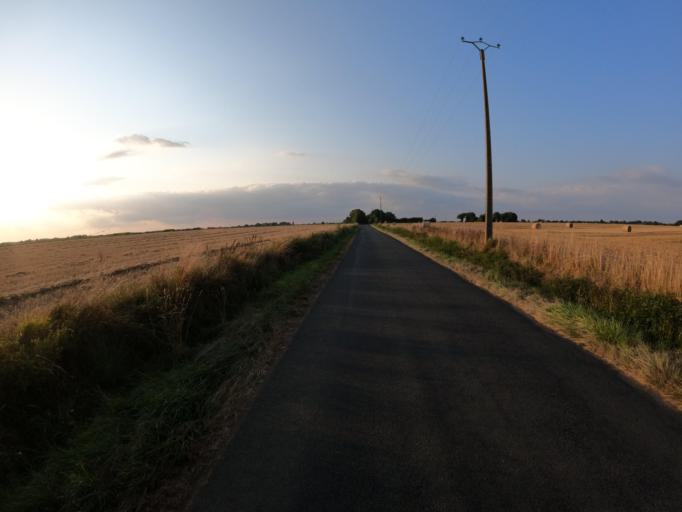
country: FR
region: Pays de la Loire
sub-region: Departement de la Sarthe
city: Parce-sur-Sarthe
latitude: 47.8942
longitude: -0.2185
